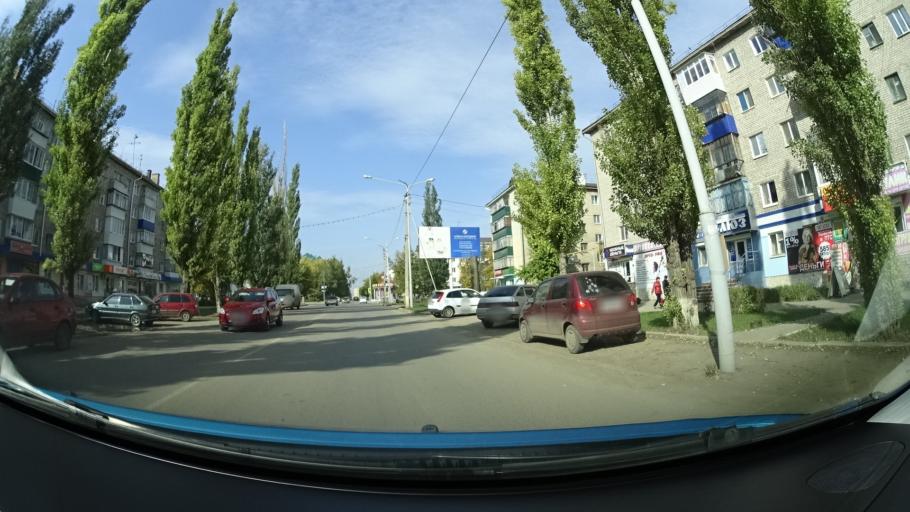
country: RU
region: Bashkortostan
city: Tuymazy
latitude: 54.6021
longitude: 53.7013
